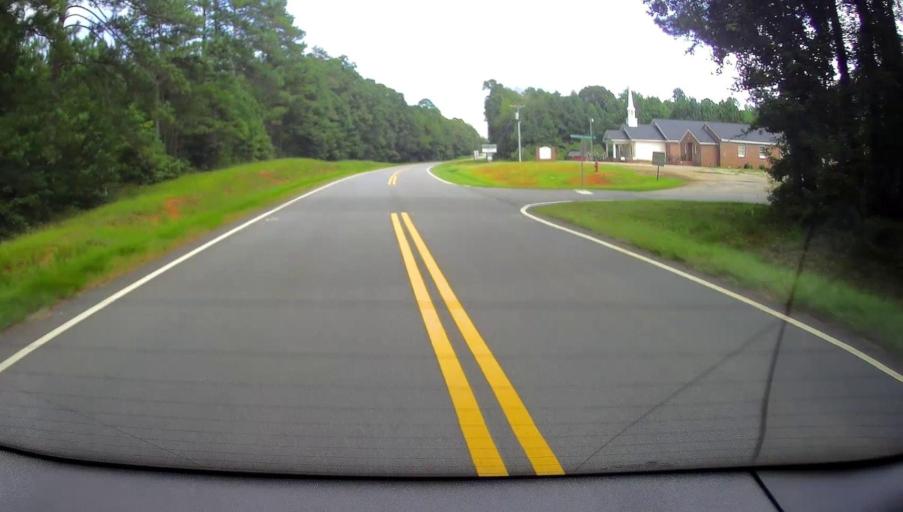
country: US
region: Georgia
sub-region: Bibb County
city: West Point
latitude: 32.8654
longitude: -83.8872
